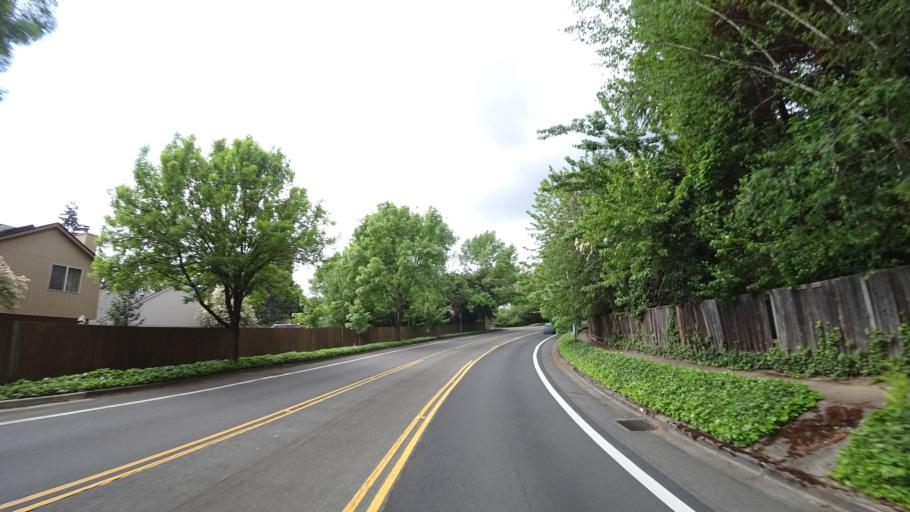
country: US
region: Oregon
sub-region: Washington County
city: Beaverton
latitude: 45.4536
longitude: -122.8222
